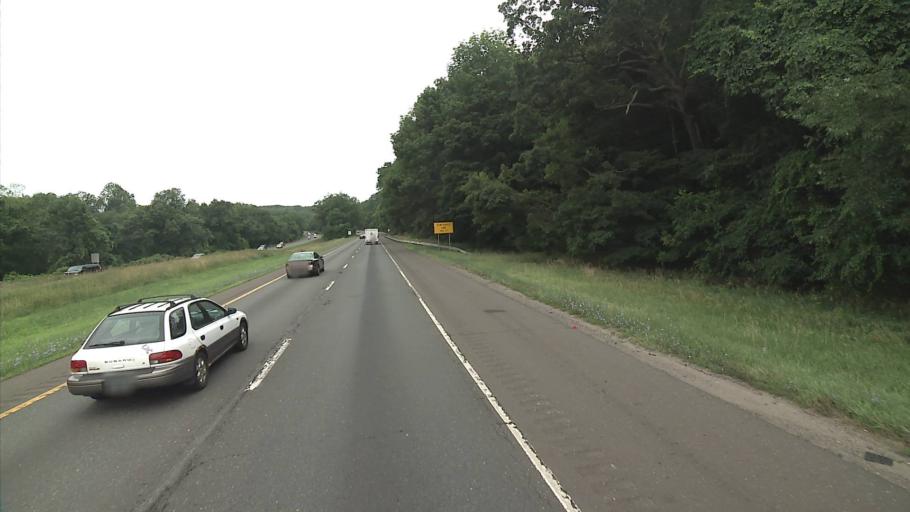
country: US
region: Connecticut
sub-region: Fairfield County
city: Newtown
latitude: 41.4274
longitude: -73.3086
